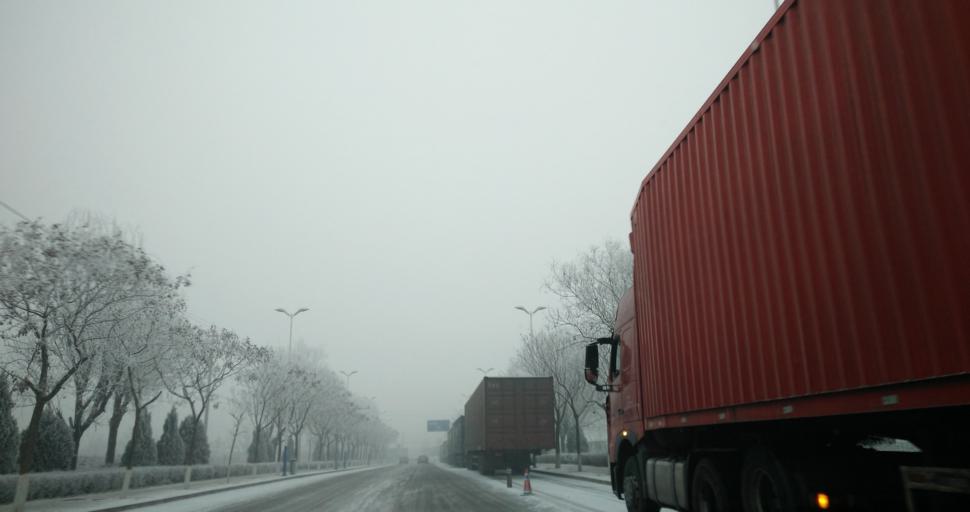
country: CN
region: Beijing
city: Yinghai
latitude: 39.7002
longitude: 116.4124
